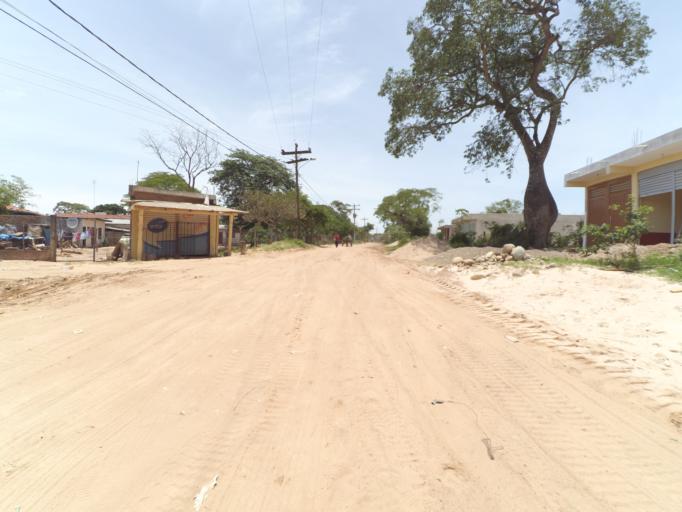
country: BO
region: Santa Cruz
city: Santa Cruz de la Sierra
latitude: -17.8221
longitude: -63.2508
